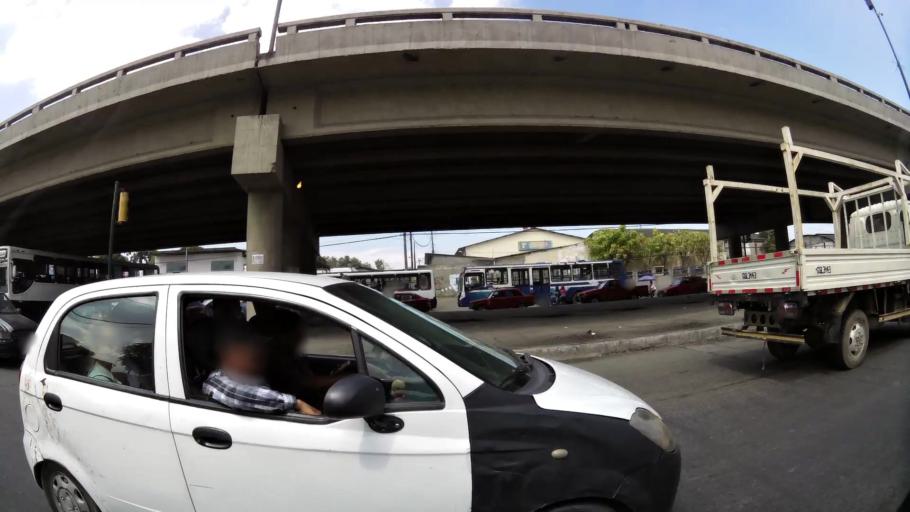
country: EC
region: Guayas
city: Guayaquil
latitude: -2.1295
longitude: -79.9331
